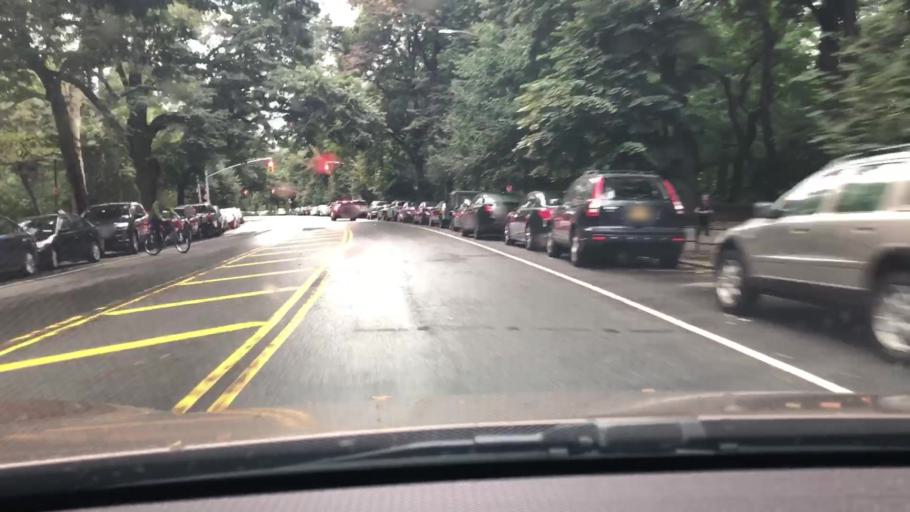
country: US
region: New York
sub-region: New York County
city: Manhattan
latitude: 40.8001
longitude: -73.9722
